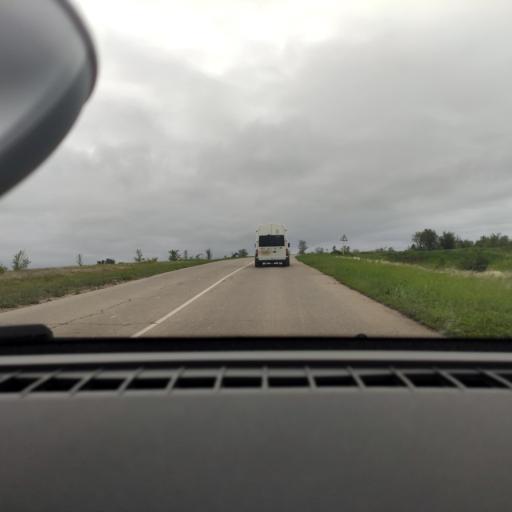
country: RU
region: Samara
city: Spiridonovka
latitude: 53.0597
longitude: 50.4685
